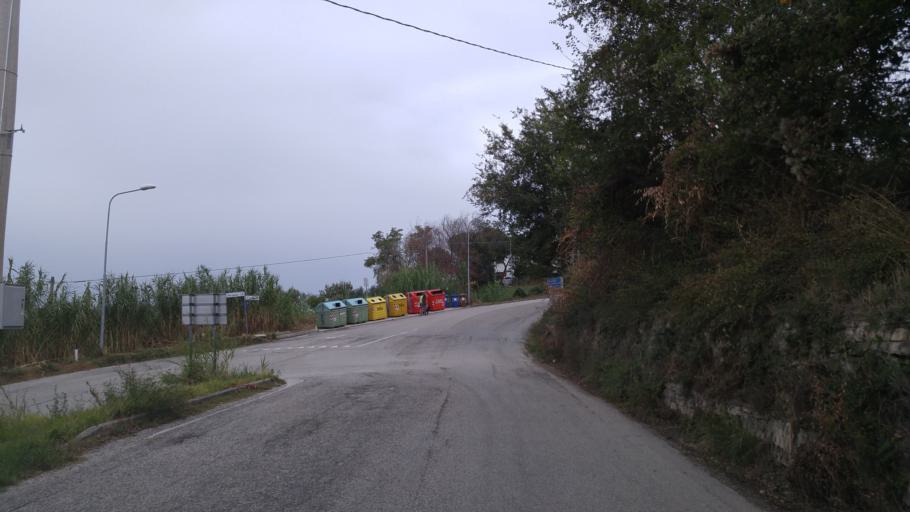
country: IT
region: The Marches
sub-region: Provincia di Pesaro e Urbino
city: Mombaroccio
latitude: 43.7931
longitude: 12.8748
